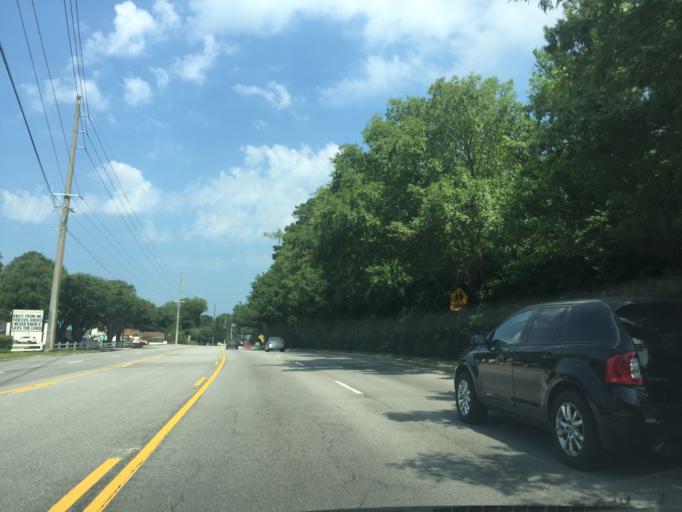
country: US
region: Georgia
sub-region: Chatham County
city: Isle of Hope
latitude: 31.9915
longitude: -81.0946
